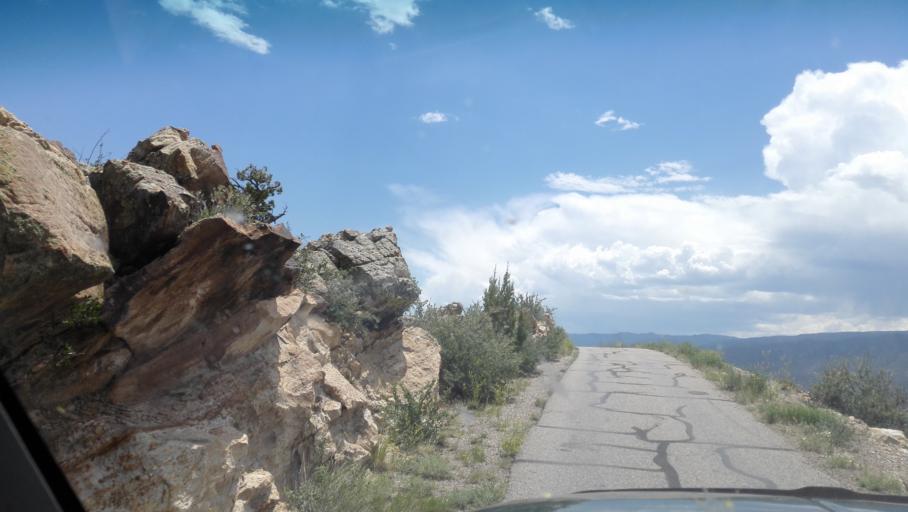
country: US
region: Colorado
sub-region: Fremont County
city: Canon City
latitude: 38.4602
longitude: -105.2511
